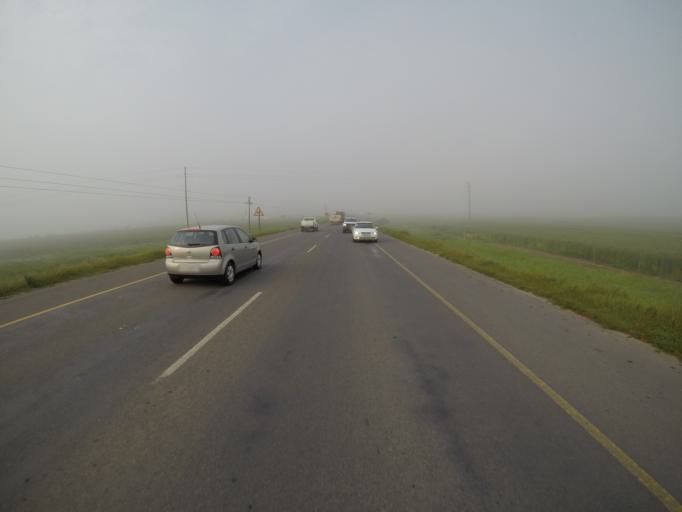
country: ZA
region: Western Cape
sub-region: City of Cape Town
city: Kraaifontein
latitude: -33.7826
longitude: 18.7046
